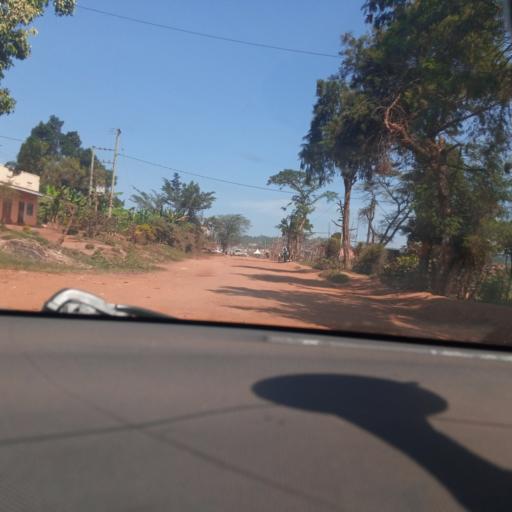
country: UG
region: Central Region
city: Masaka
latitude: -0.3103
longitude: 31.7569
